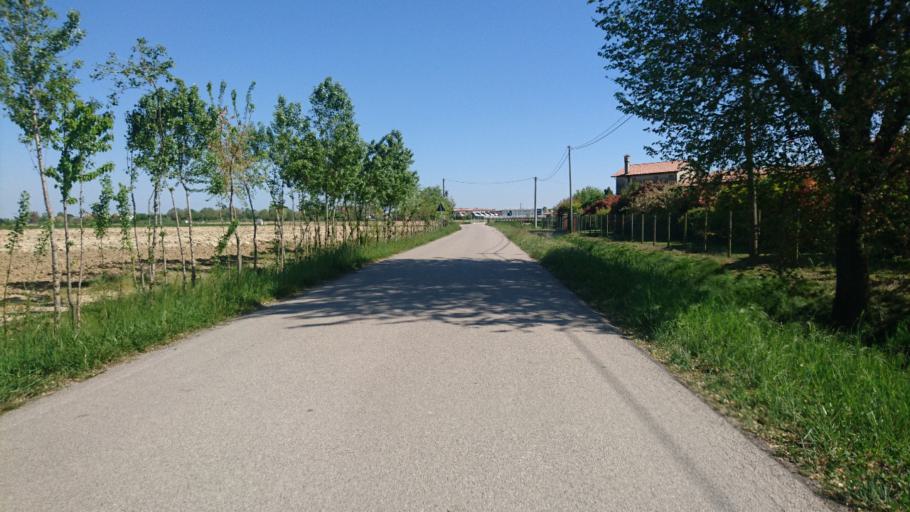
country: IT
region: Veneto
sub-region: Provincia di Venezia
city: Marcon-Gaggio-Colmello
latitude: 45.5694
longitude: 12.2898
